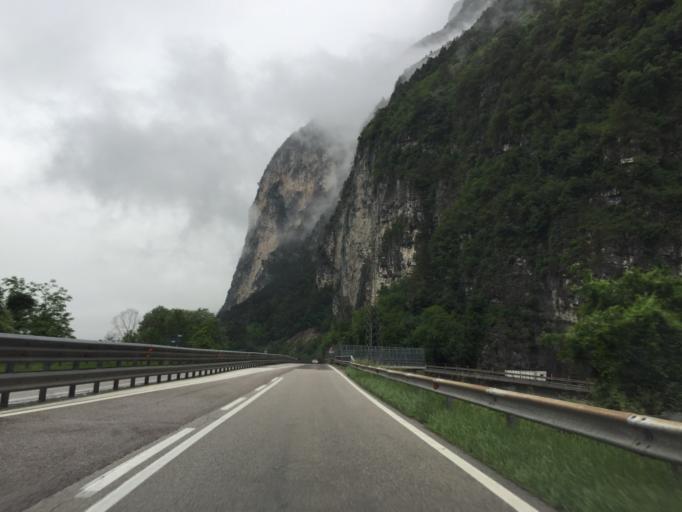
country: IT
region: Trentino-Alto Adige
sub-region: Provincia di Trento
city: Grigno
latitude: 46.0170
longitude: 11.6108
